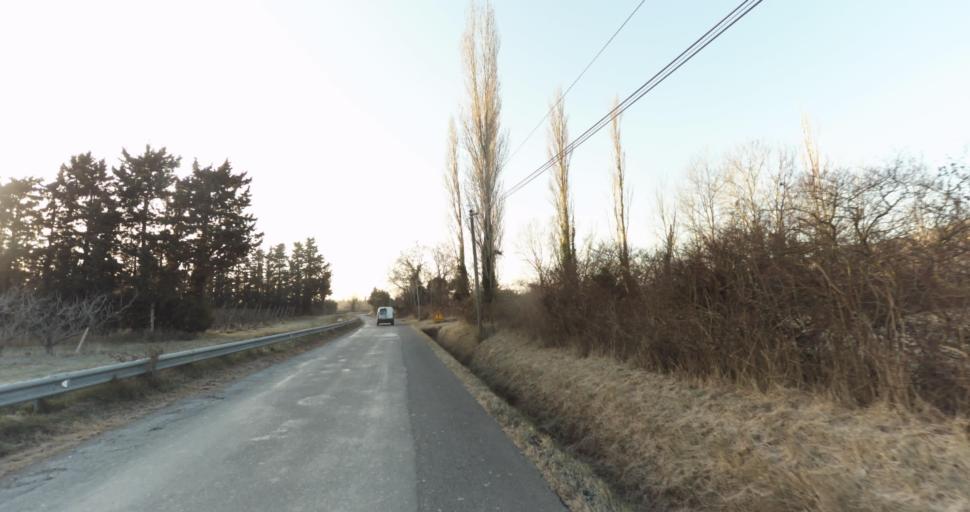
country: FR
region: Provence-Alpes-Cote d'Azur
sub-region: Departement des Bouches-du-Rhone
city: Barbentane
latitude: 43.8960
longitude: 4.7713
